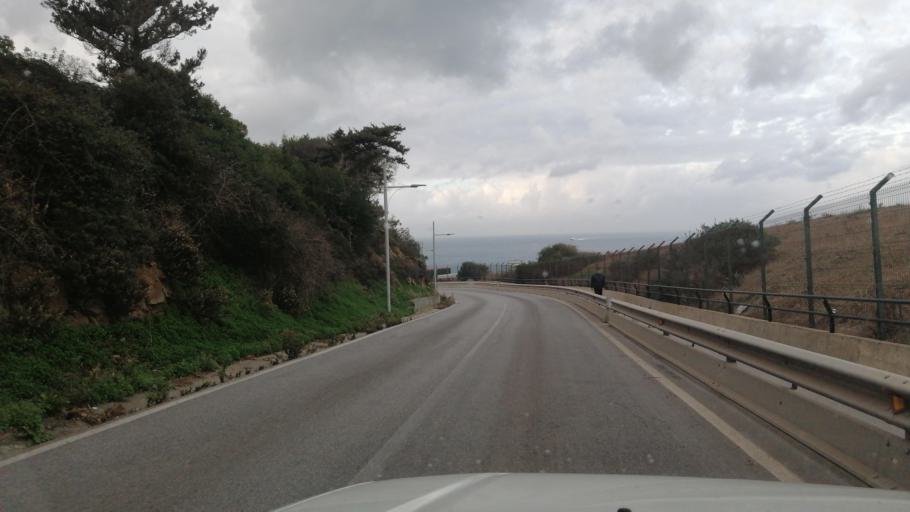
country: ES
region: Ceuta
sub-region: Ceuta
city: Ceuta
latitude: 35.9012
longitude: -5.2864
